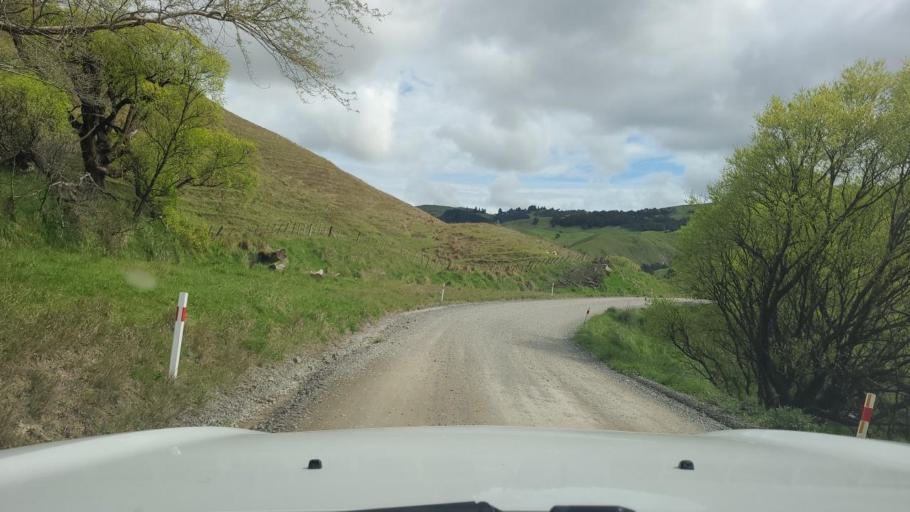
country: NZ
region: Wellington
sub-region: South Wairarapa District
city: Waipawa
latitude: -41.2931
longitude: 175.6445
